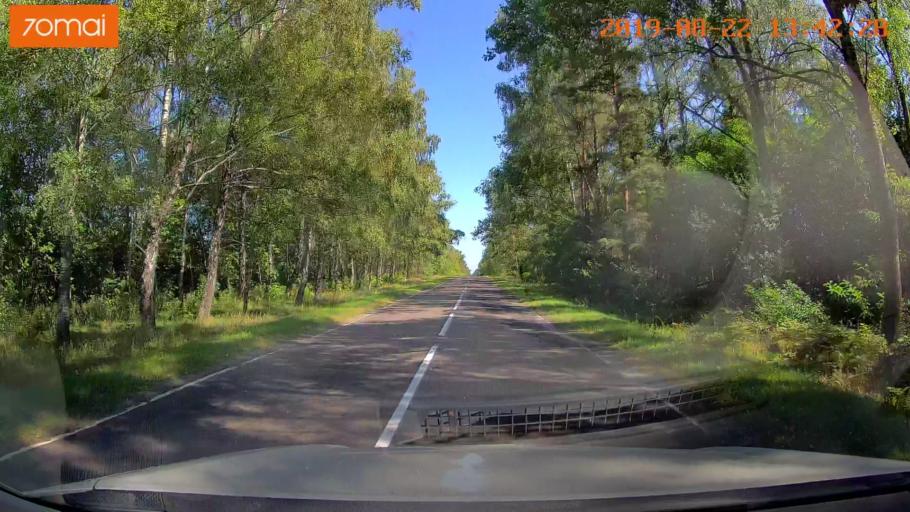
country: BY
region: Mogilev
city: Asipovichy
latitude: 53.2411
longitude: 28.4151
